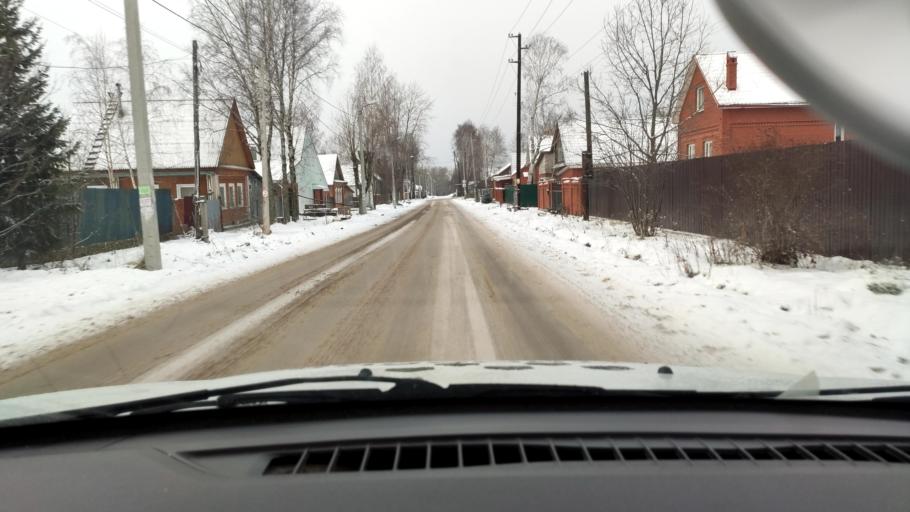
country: RU
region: Perm
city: Polazna
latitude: 58.1177
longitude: 56.3971
